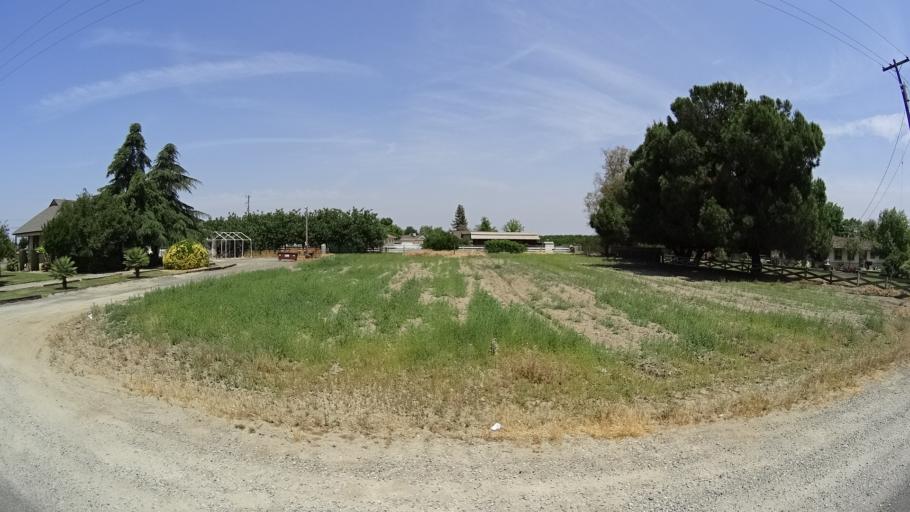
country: US
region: California
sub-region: Kings County
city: Lemoore
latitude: 36.3135
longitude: -119.7620
